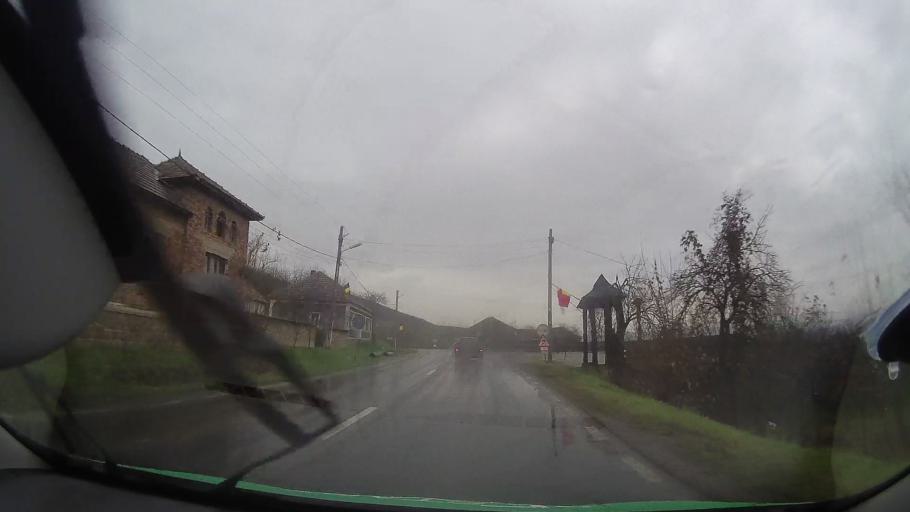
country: RO
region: Bihor
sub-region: Comuna Sambata
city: Sambata
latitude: 46.7621
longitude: 22.1901
